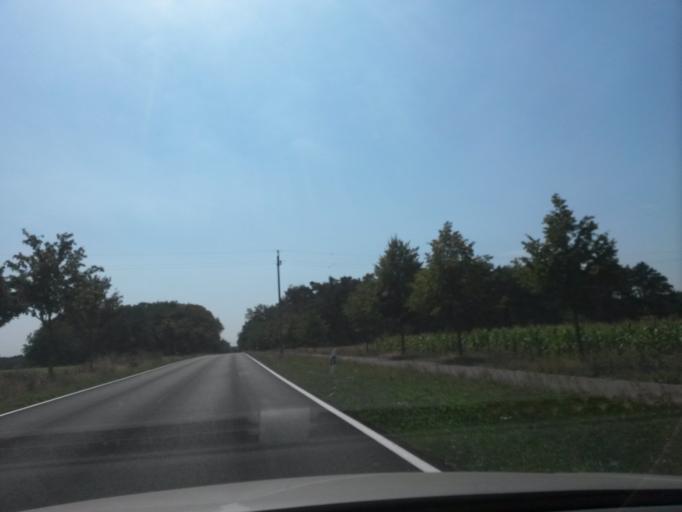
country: DE
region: Saxony-Anhalt
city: Jerichow
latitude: 52.4004
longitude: 11.9960
